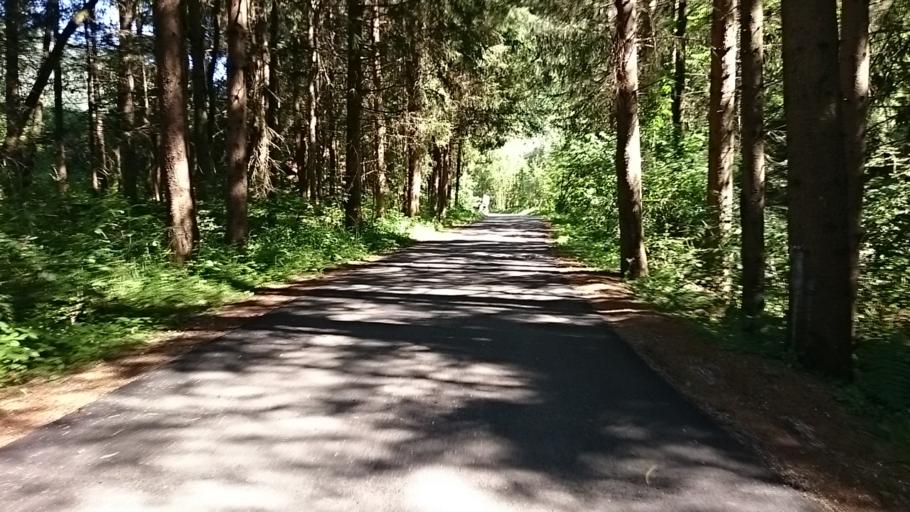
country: IT
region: Trentino-Alto Adige
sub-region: Bolzano
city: Perca
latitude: 46.7864
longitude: 11.9961
